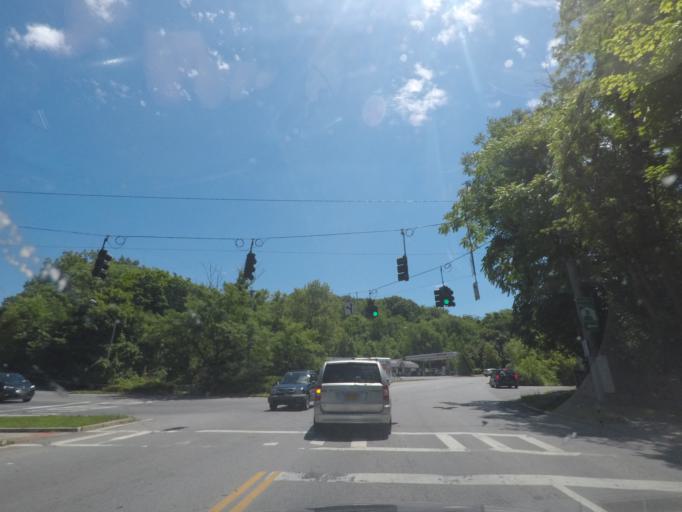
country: US
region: New York
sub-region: Rensselaer County
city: Troy
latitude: 42.7047
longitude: -73.6967
